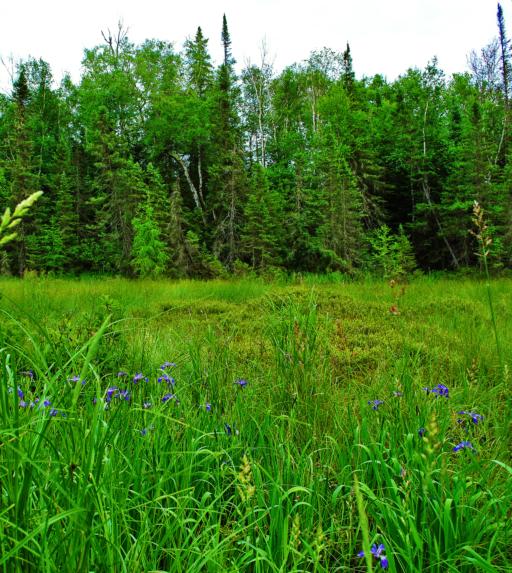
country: US
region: Wisconsin
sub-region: Vilas County
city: Eagle River
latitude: 45.7149
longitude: -89.1561
